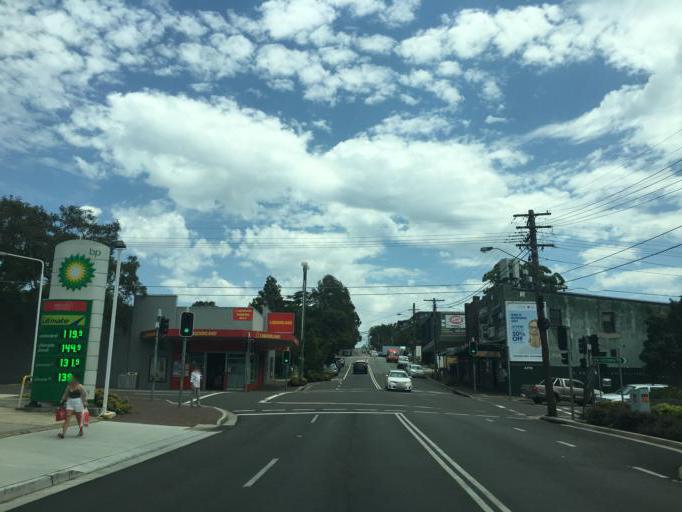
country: AU
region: New South Wales
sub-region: Canada Bay
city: Rhodes
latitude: -33.8238
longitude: 151.1088
